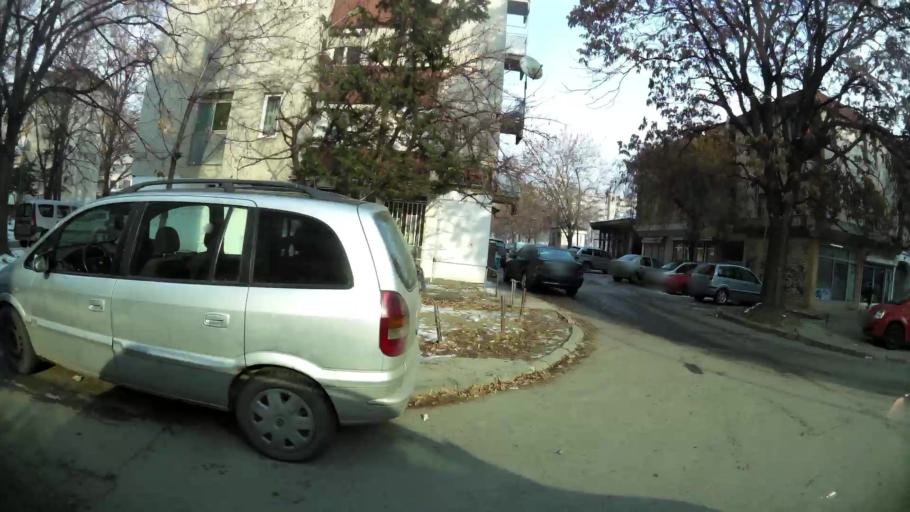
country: MK
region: Cair
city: Cair
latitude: 42.0156
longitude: 21.4329
